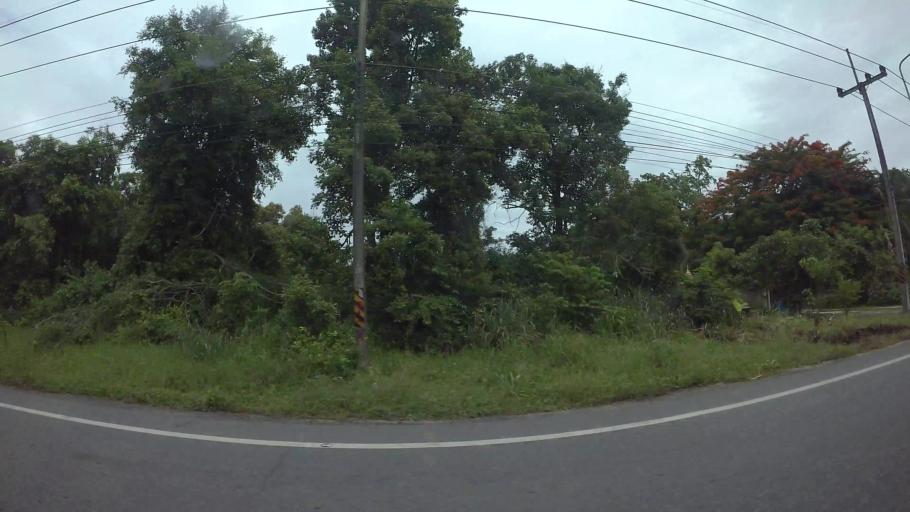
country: TH
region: Chon Buri
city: Si Racha
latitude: 13.1807
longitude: 100.9720
